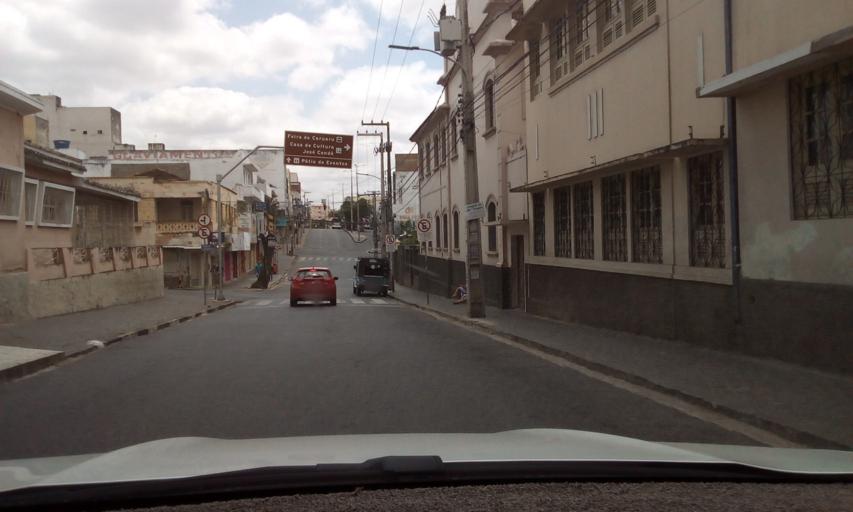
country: BR
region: Pernambuco
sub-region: Caruaru
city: Caruaru
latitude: -8.2873
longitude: -35.9735
